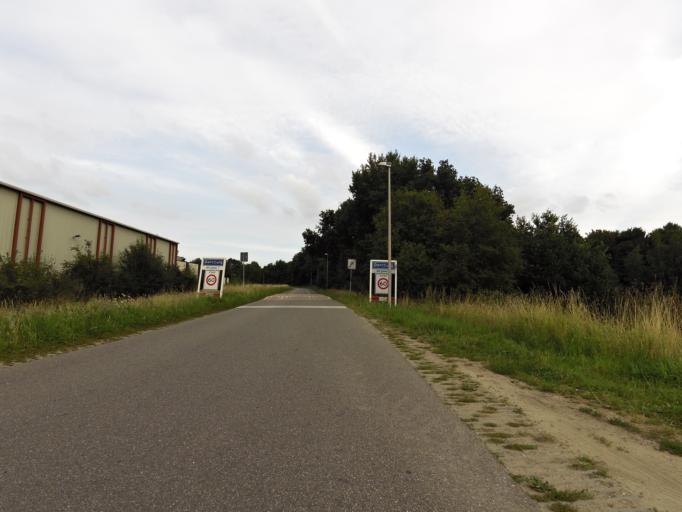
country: NL
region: Gelderland
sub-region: Gemeente Doesburg
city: Doesburg
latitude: 52.0004
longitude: 6.1413
